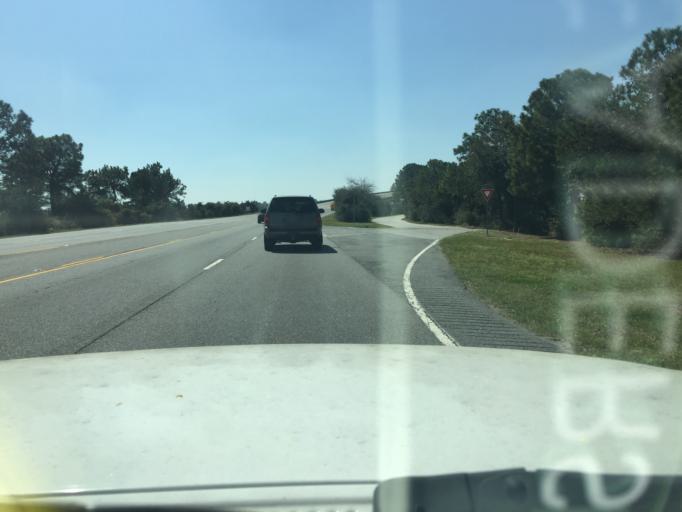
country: US
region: Georgia
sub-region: Chatham County
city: Thunderbolt
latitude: 32.0354
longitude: -81.0401
